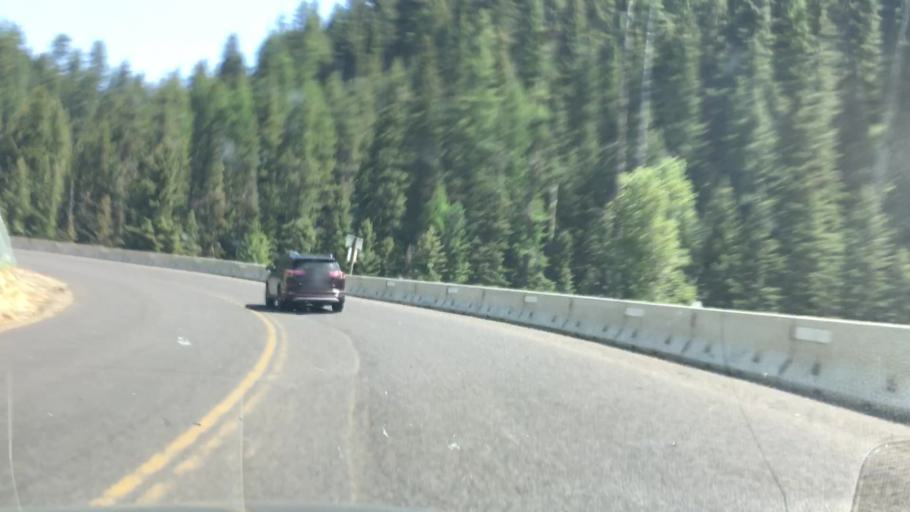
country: US
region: Idaho
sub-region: Valley County
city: McCall
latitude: 44.9644
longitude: -116.1776
